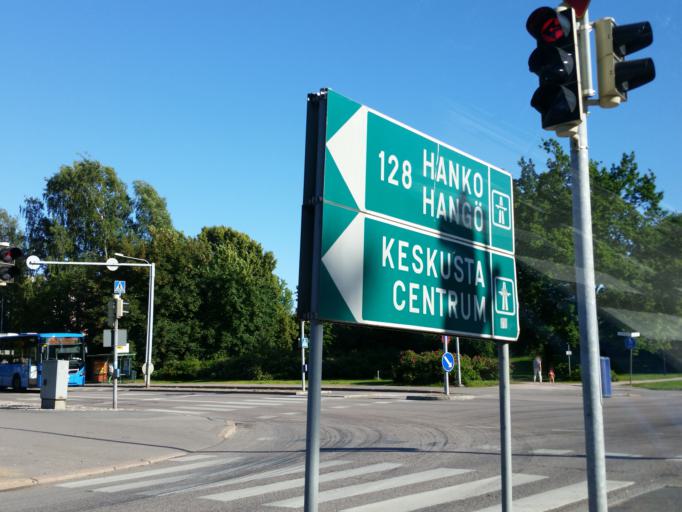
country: FI
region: Uusimaa
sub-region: Helsinki
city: Teekkarikylae
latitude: 60.1612
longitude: 24.8754
